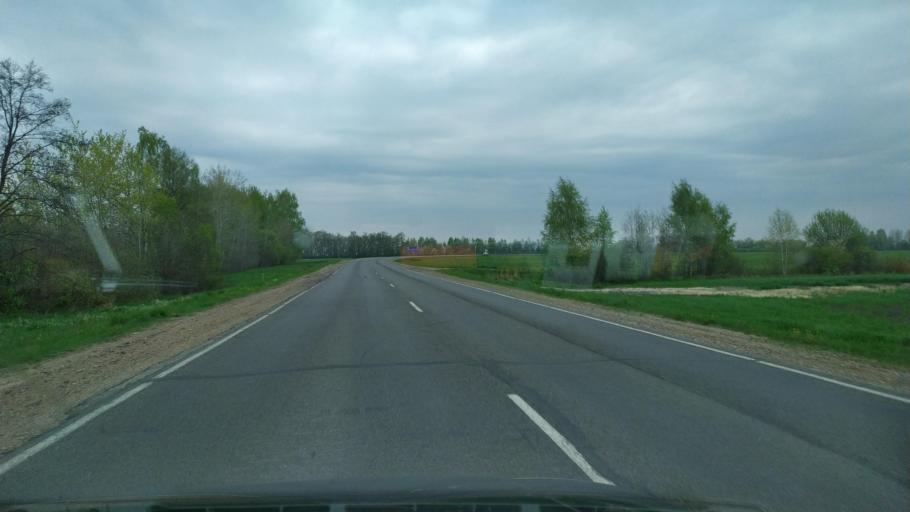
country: BY
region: Brest
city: Horad Kobryn
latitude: 52.2379
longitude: 24.4093
